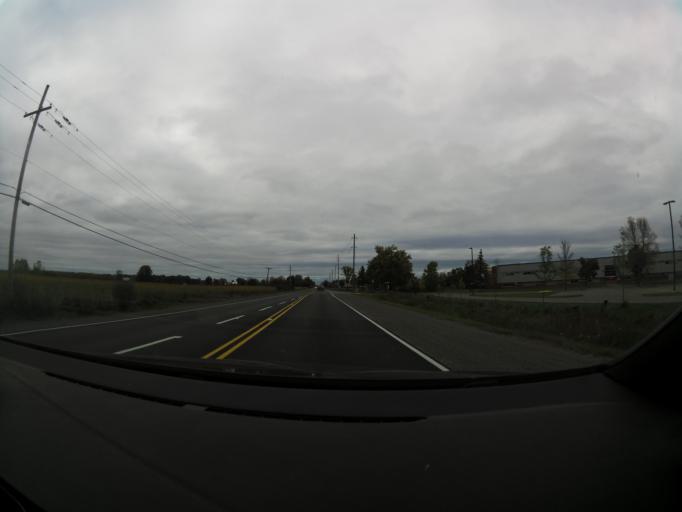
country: CA
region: Ontario
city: Bells Corners
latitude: 45.4331
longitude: -76.0353
